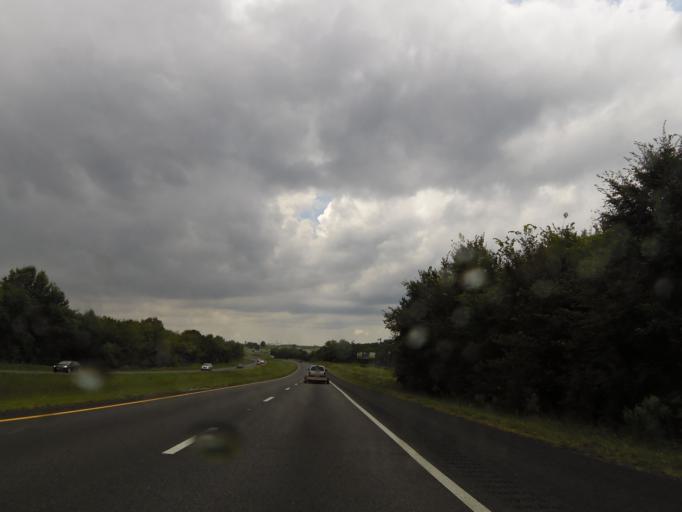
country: US
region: Tennessee
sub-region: Wilson County
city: Watertown
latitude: 36.1872
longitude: -86.1634
